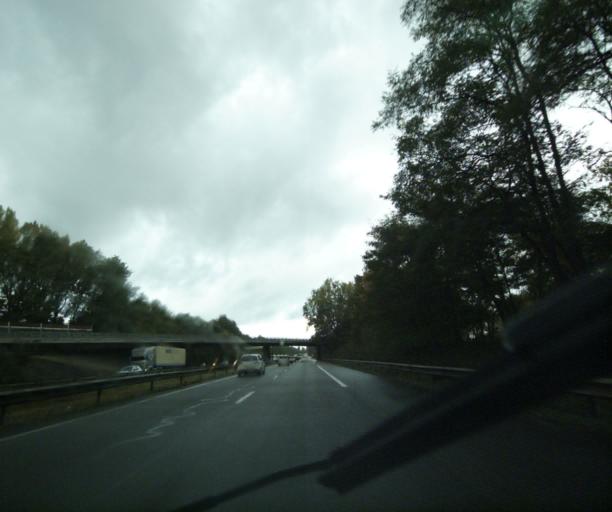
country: FR
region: Nord-Pas-de-Calais
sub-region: Departement du Nord
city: Mouvaux
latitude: 50.7188
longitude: 3.1242
